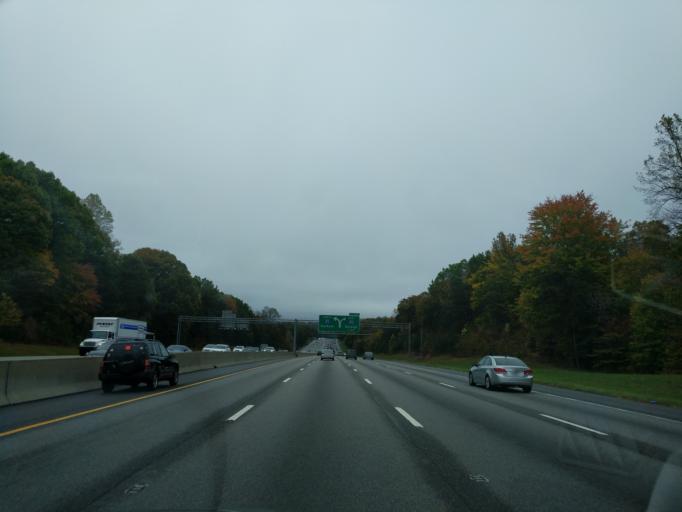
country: US
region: North Carolina
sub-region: Orange County
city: Hillsborough
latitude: 36.0684
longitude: -79.1494
